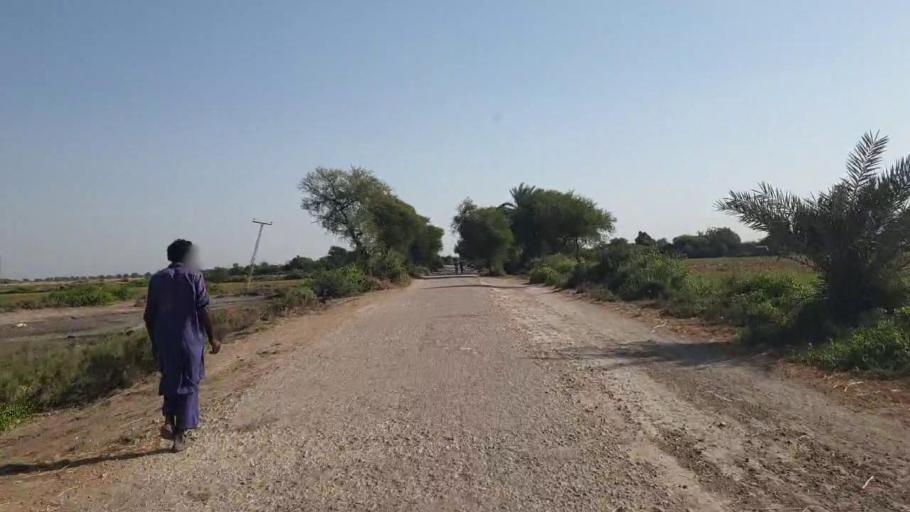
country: PK
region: Sindh
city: Matli
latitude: 25.0572
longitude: 68.7185
